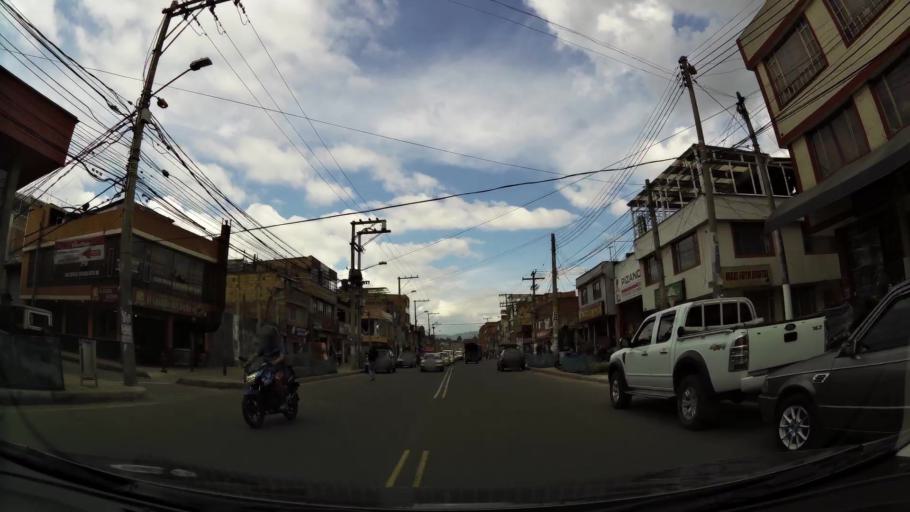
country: CO
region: Cundinamarca
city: Cota
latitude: 4.7403
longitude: -74.0946
